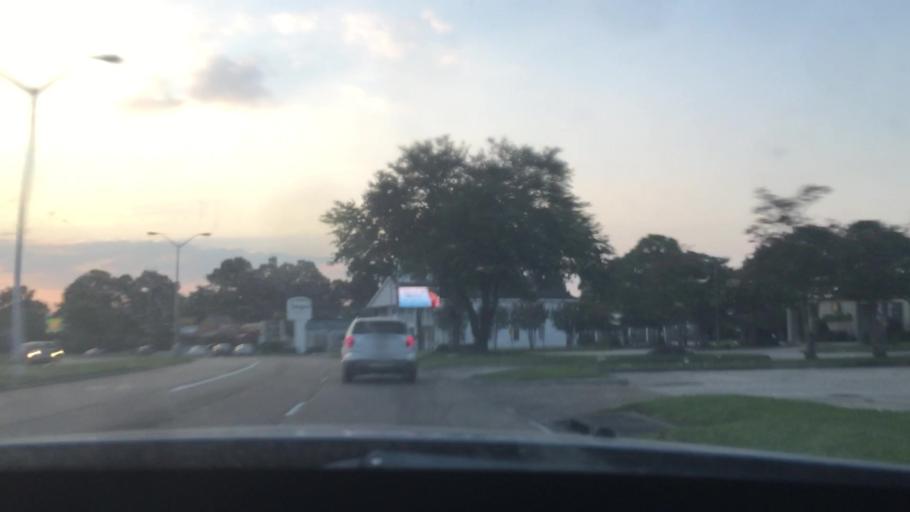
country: US
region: Louisiana
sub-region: East Baton Rouge Parish
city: Westminster
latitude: 30.4255
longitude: -91.0519
